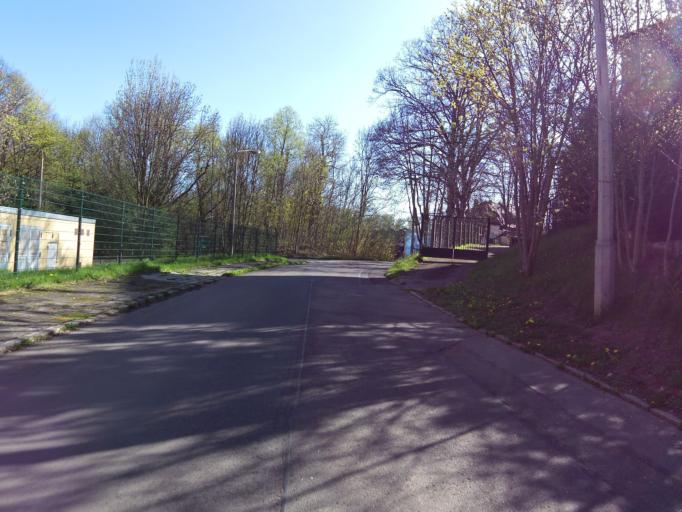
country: DE
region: Thuringia
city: Gotha
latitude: 50.9368
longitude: 10.7136
